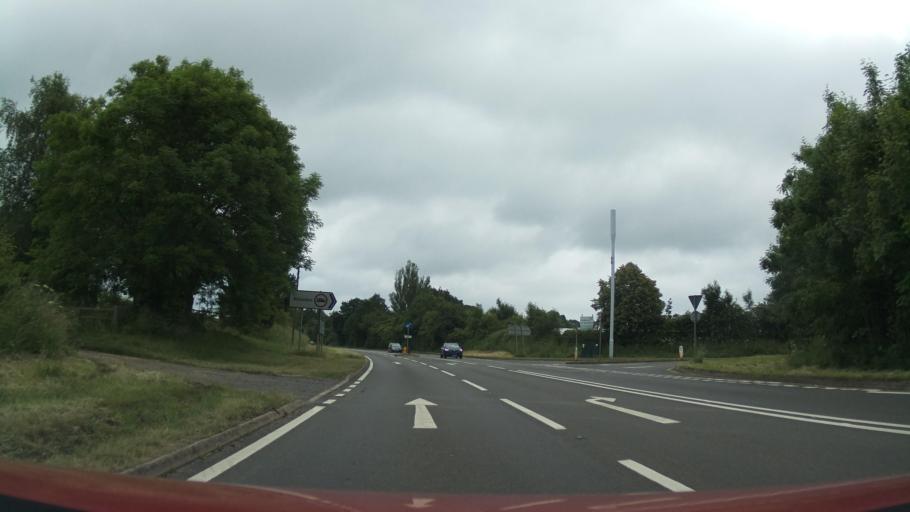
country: GB
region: England
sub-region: Leicestershire
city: Houghton on the Hill
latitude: 52.6200
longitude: -0.9584
